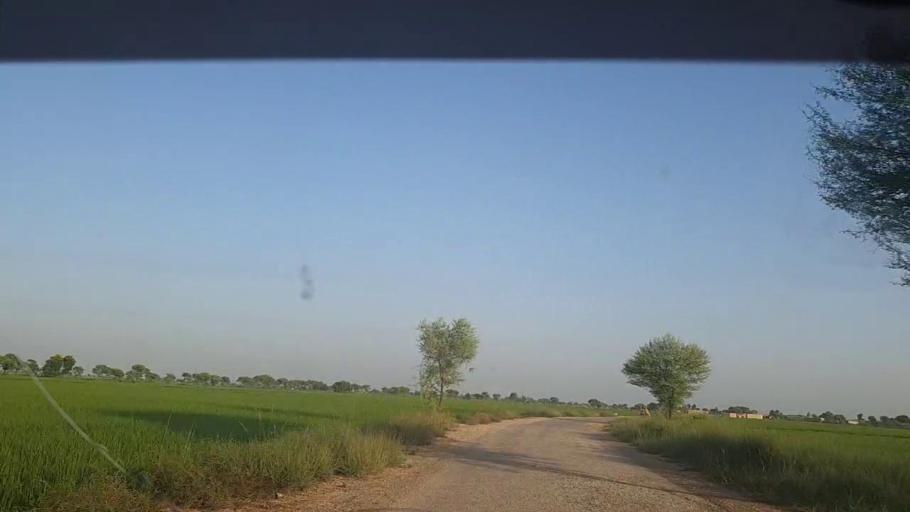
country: PK
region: Sindh
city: Thul
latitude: 28.1353
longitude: 68.8886
